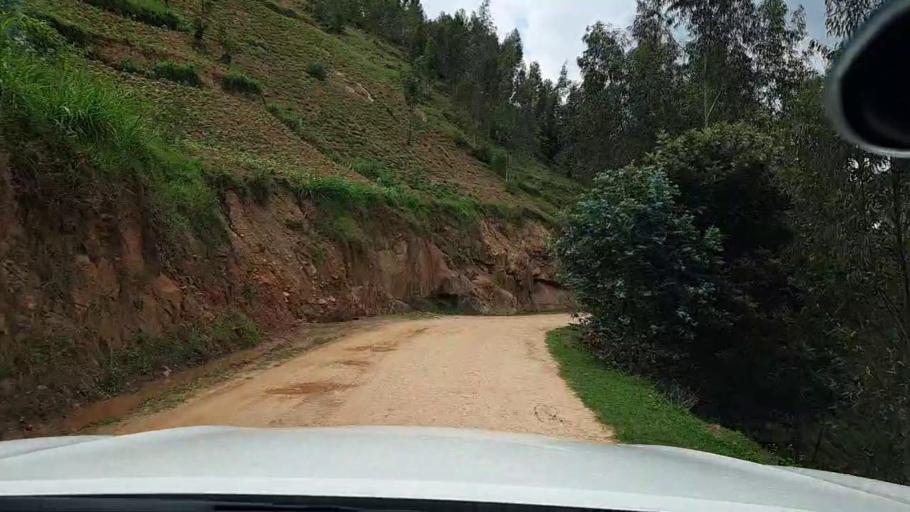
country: RW
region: Western Province
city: Kibuye
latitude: -2.1201
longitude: 29.4243
